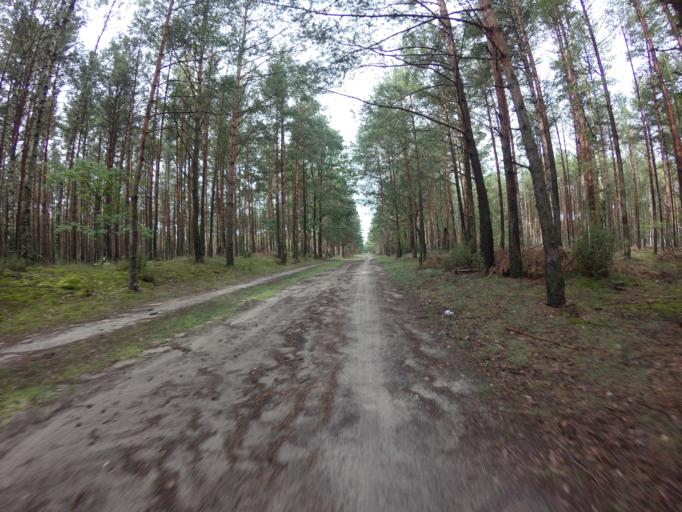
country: PL
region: Kujawsko-Pomorskie
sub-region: Powiat bydgoski
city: Osielsko
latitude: 53.1532
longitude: 18.0950
